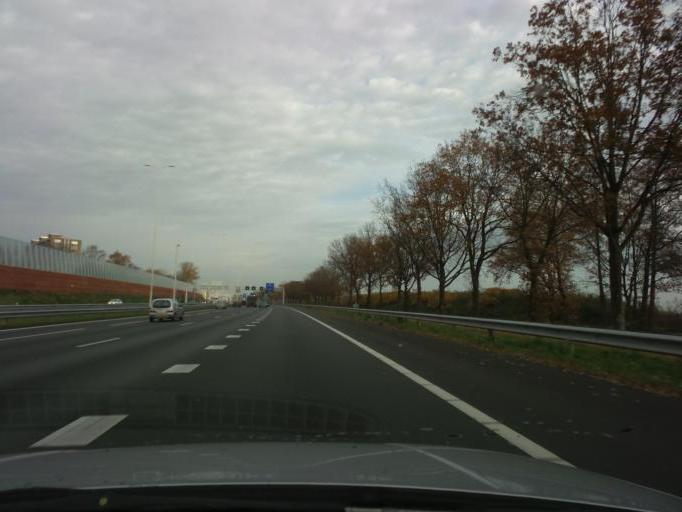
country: NL
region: Utrecht
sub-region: Gemeente Amersfoort
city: Randenbroek
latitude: 52.1506
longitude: 5.4156
